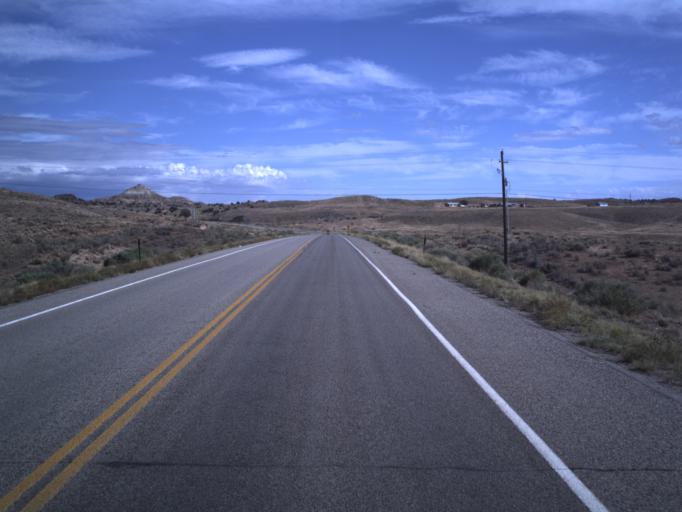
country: US
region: Colorado
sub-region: Montezuma County
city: Towaoc
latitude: 37.1978
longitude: -109.1504
